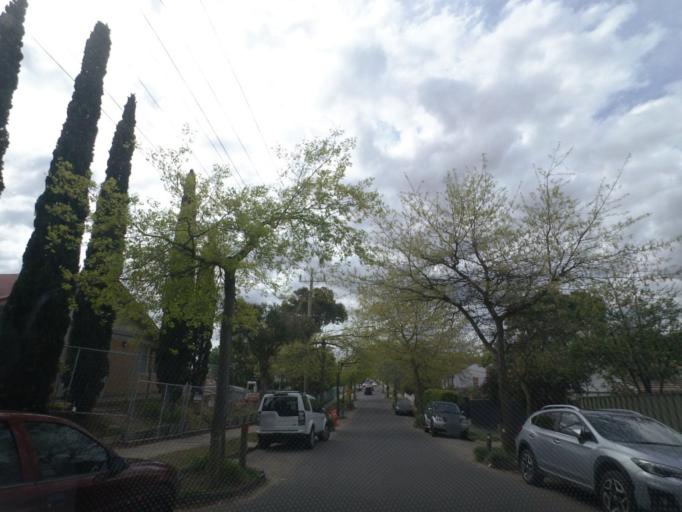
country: AU
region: Victoria
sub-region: Boroondara
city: Kew East
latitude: -37.8083
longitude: 145.0537
